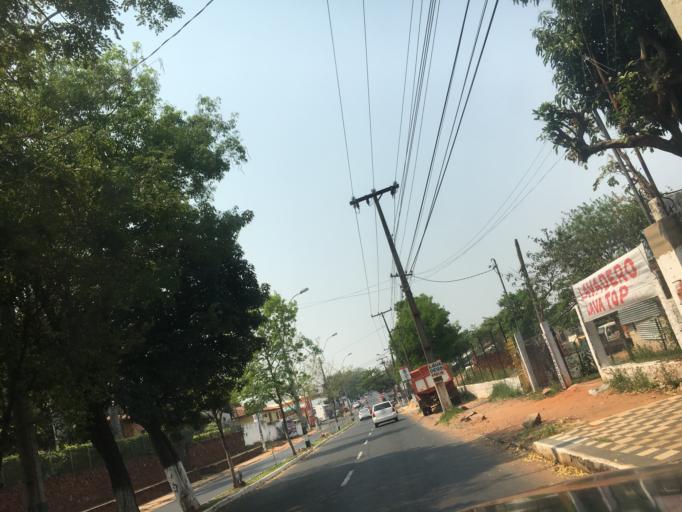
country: PY
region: Central
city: Villa Elisa
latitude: -25.3775
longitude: -57.5858
